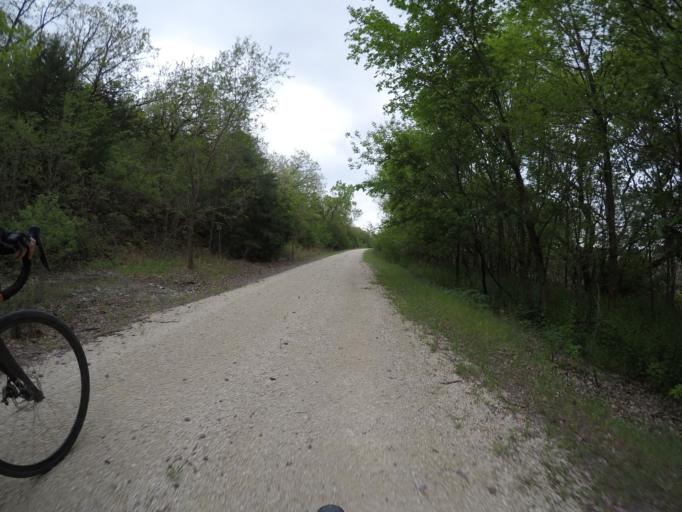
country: US
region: Nebraska
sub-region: Gage County
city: Wymore
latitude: 40.1319
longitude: -96.6442
